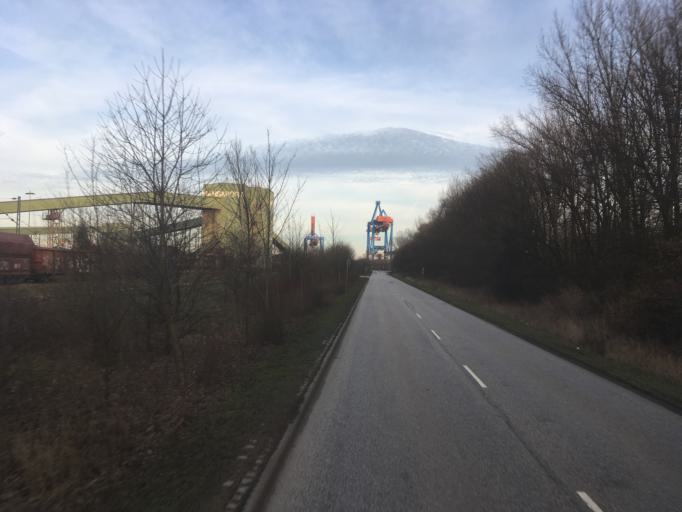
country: DE
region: Hamburg
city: Altona
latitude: 53.5112
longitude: 9.9267
